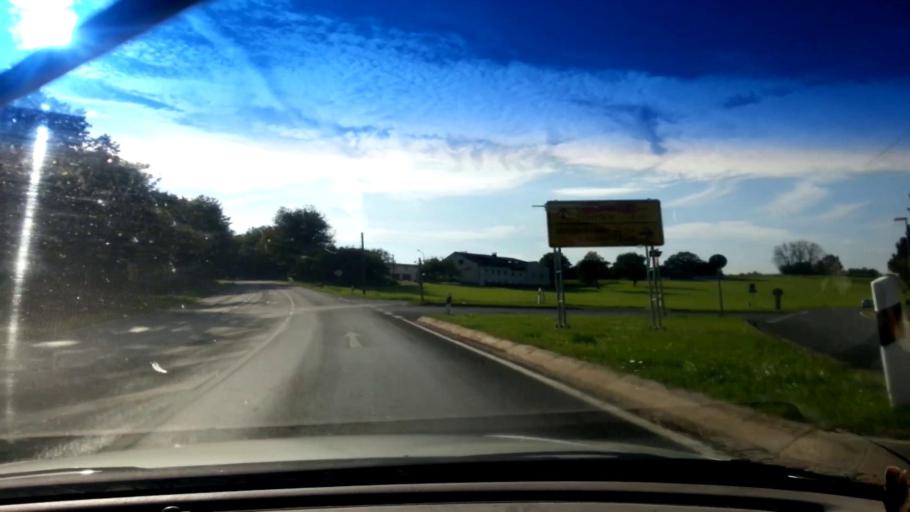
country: DE
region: Bavaria
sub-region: Upper Franconia
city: Lauter
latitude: 49.9681
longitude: 10.7963
